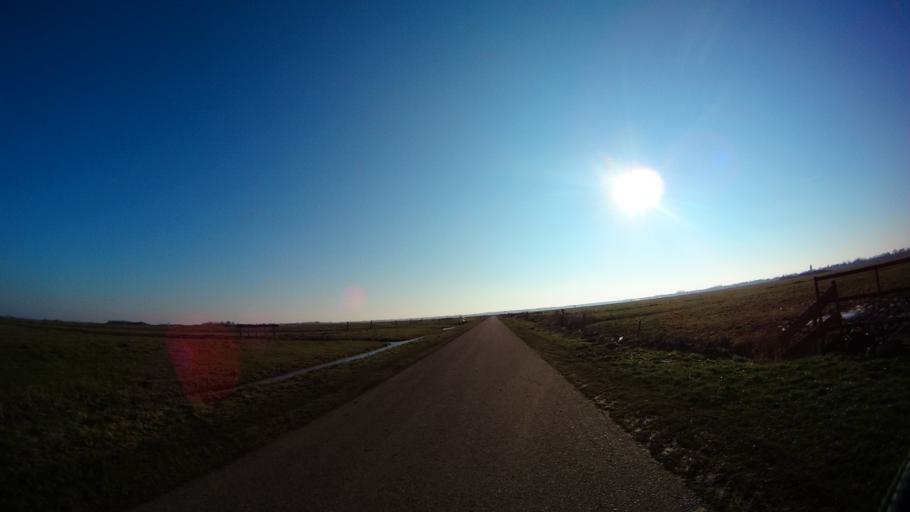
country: NL
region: North Holland
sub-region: Gemeente Blaricum
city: Blaricum
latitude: 52.2610
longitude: 5.2895
